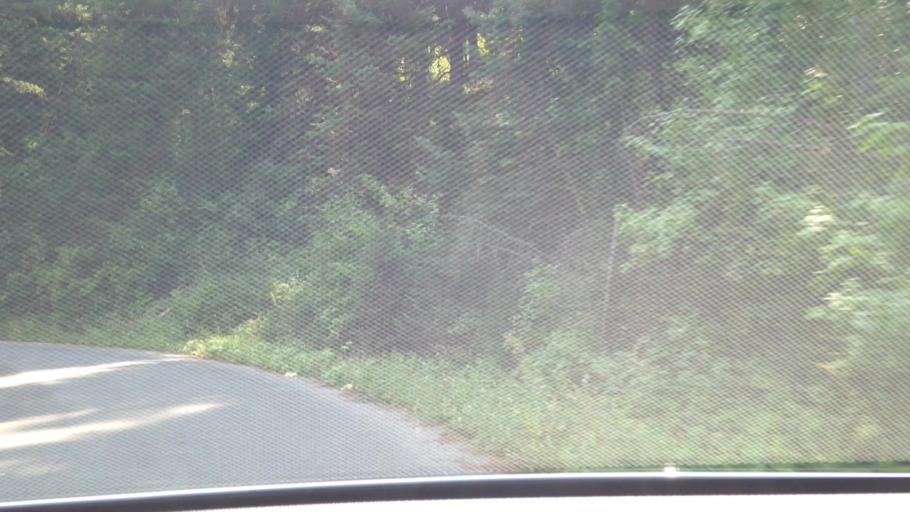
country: US
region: Utah
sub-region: Summit County
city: Summit Park
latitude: 40.6890
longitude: -111.6627
